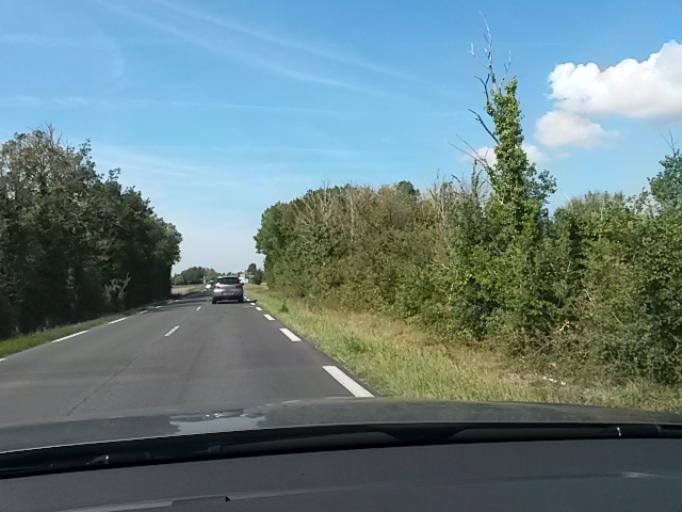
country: FR
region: Poitou-Charentes
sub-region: Departement de la Charente-Maritime
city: Saint-Denis-d'Oleron
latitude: 45.9643
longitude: -1.3451
